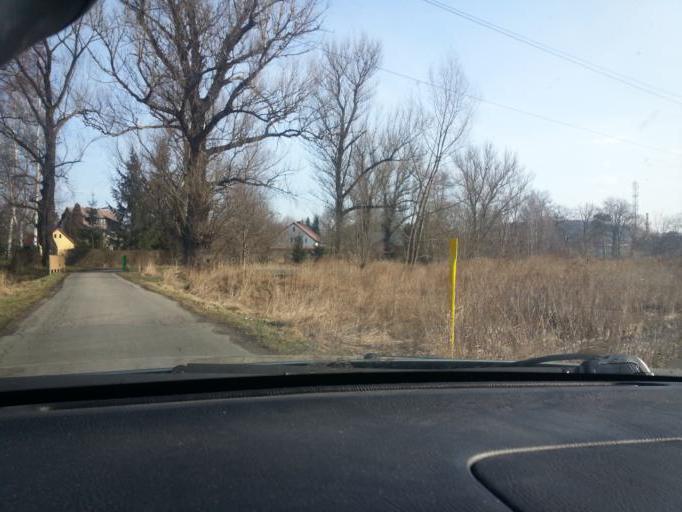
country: PL
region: Lower Silesian Voivodeship
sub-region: Jelenia Gora
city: Cieplice Slaskie Zdroj
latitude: 50.8783
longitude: 15.7028
